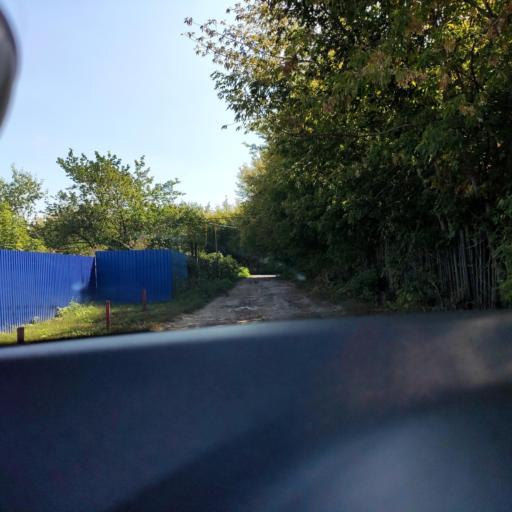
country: RU
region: Samara
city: Smyshlyayevka
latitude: 53.2419
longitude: 50.3508
